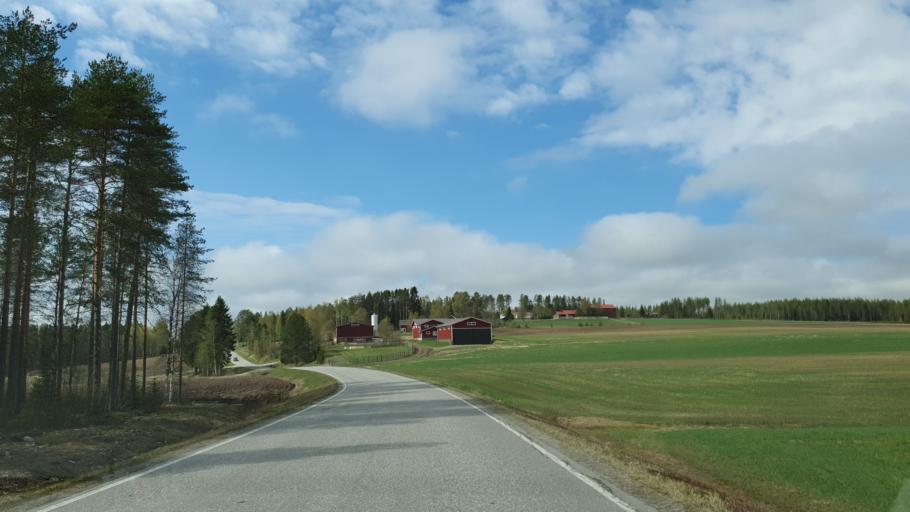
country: FI
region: Kainuu
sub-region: Kehys-Kainuu
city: Kuhmo
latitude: 64.1241
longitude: 29.6532
